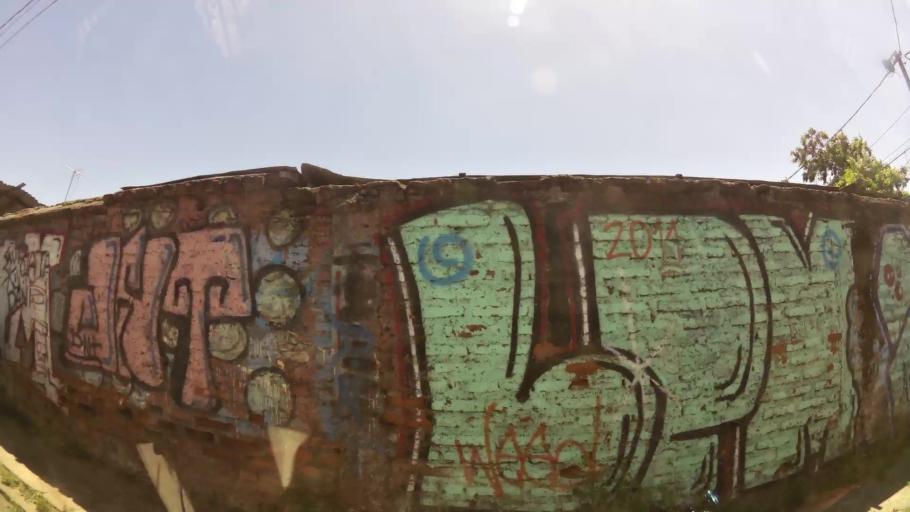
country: CL
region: Santiago Metropolitan
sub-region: Provincia de Santiago
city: La Pintana
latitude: -33.5659
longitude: -70.6666
